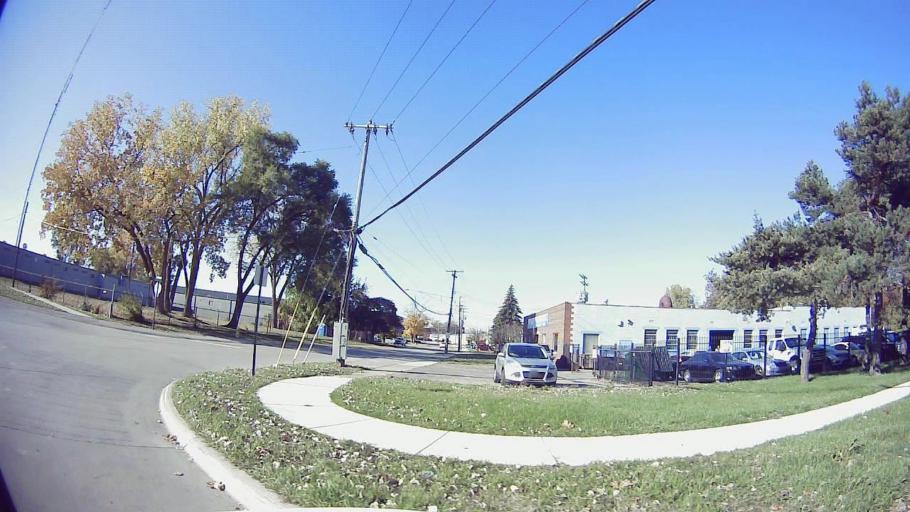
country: US
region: Michigan
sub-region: Oakland County
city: Oak Park
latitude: 42.4564
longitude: -83.1619
